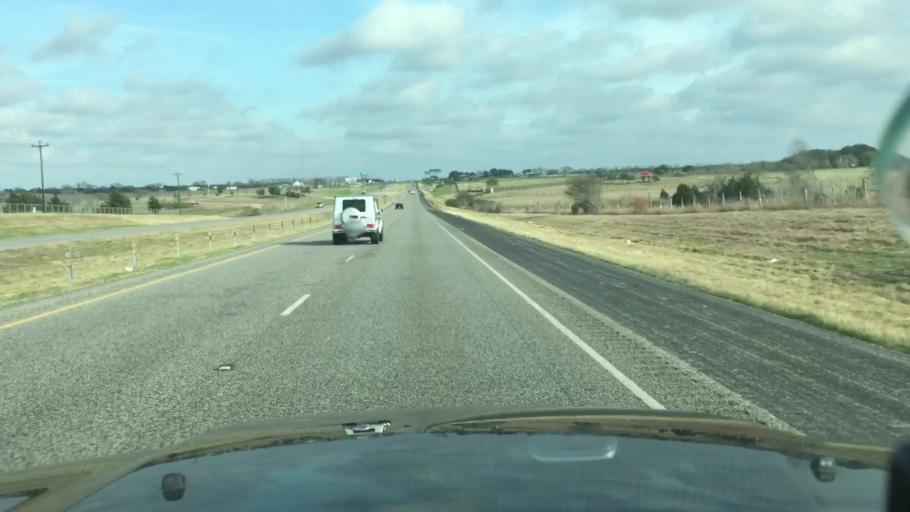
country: US
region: Texas
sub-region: Washington County
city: Brenham
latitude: 30.1392
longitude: -96.3106
